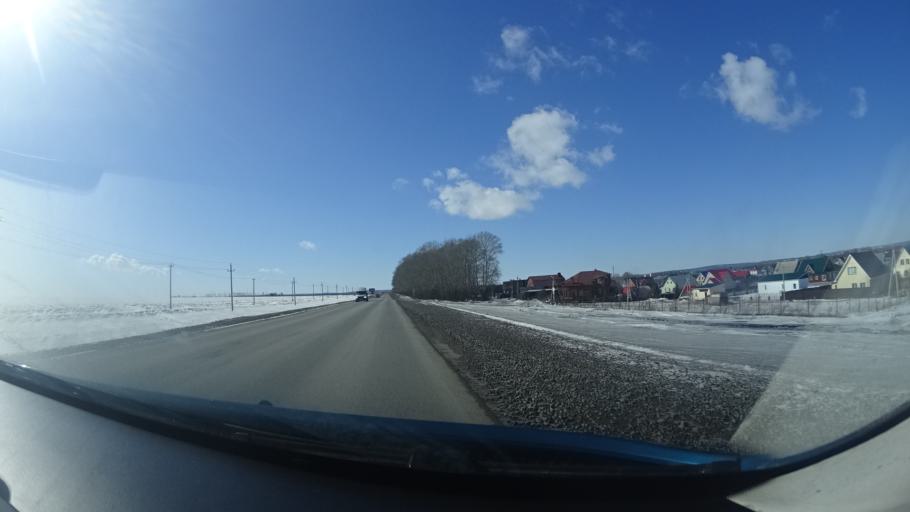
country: RU
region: Bashkortostan
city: Avdon
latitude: 54.6070
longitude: 55.8594
